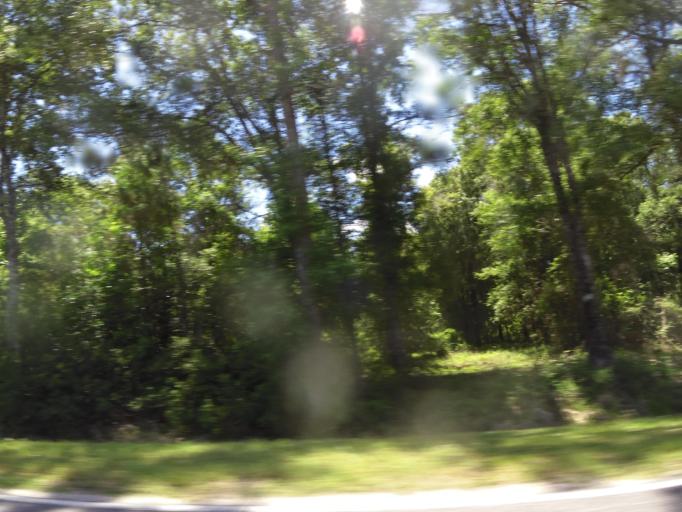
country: US
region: Florida
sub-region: Bradford County
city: Starke
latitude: 30.0247
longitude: -82.0749
